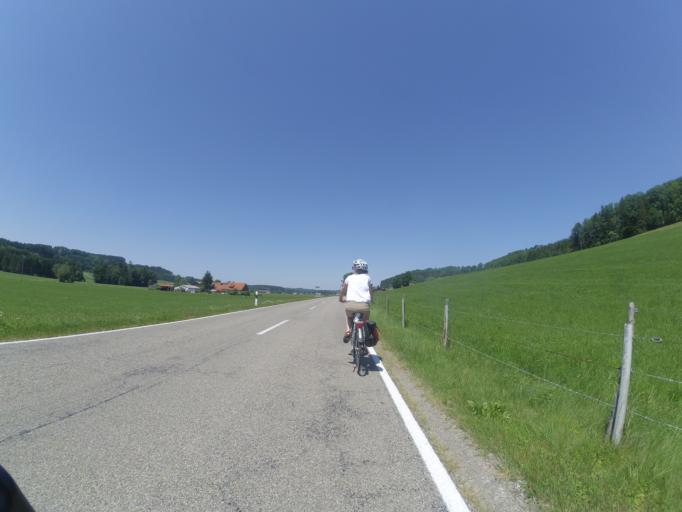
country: DE
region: Bavaria
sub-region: Swabia
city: Bohen
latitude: 47.8739
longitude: 10.3397
